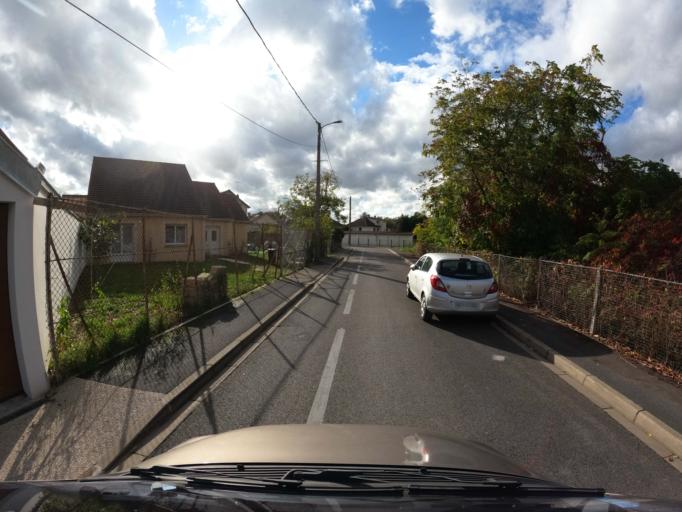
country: FR
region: Ile-de-France
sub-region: Departement de Seine-et-Marne
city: Esbly
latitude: 48.9022
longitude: 2.8092
